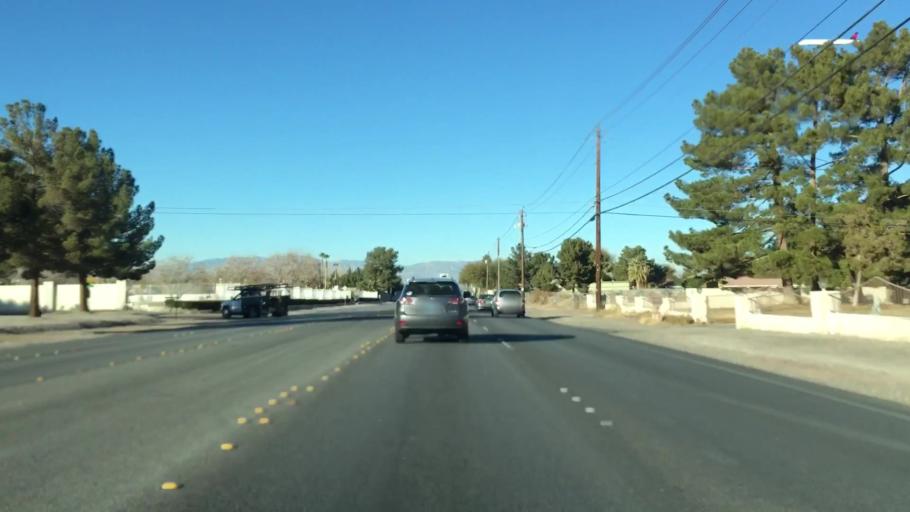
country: US
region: Nevada
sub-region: Clark County
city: Whitney
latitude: 36.0674
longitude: -115.1007
